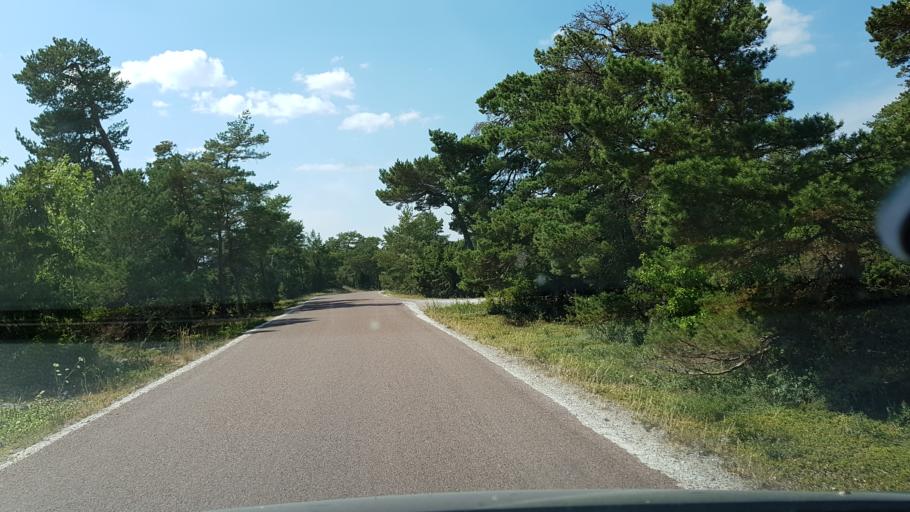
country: SE
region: Gotland
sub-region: Gotland
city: Visby
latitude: 57.6848
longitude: 18.3584
